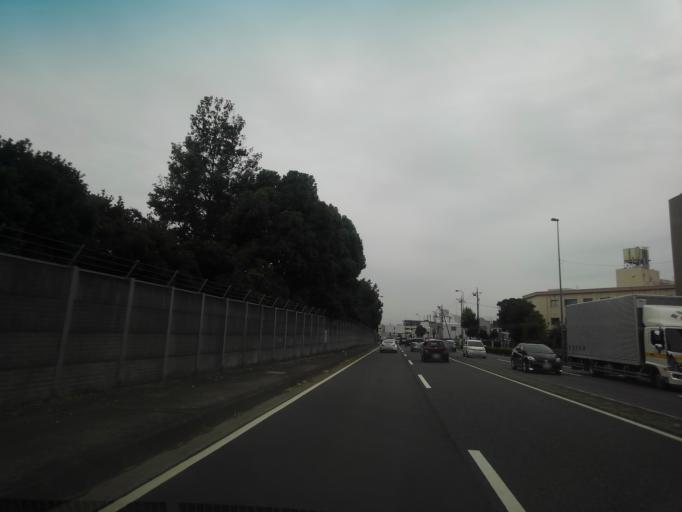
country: JP
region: Tokyo
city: Fussa
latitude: 35.7498
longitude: 139.3385
